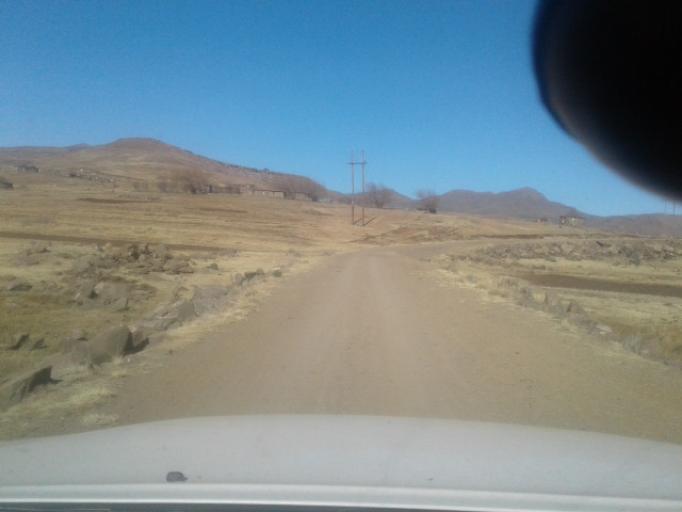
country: LS
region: Maseru
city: Nako
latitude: -29.3734
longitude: 28.0209
